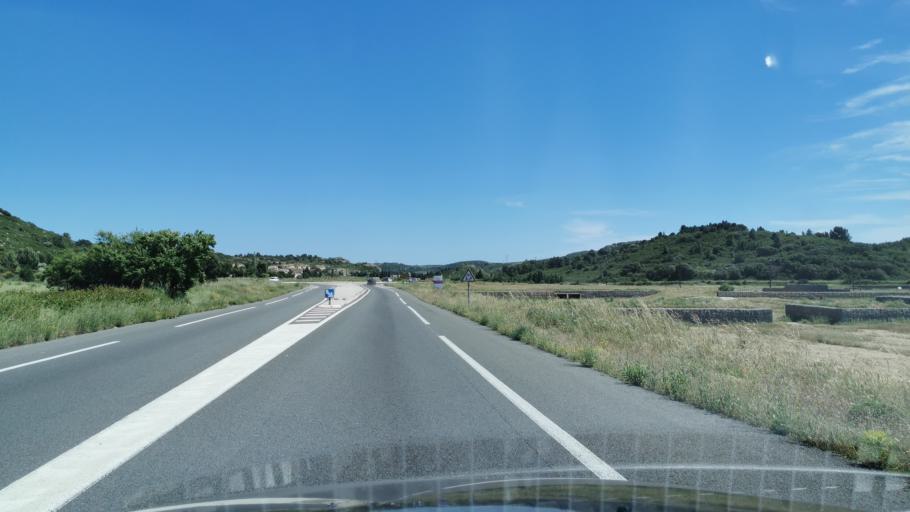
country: FR
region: Languedoc-Roussillon
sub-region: Departement de l'Aude
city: Nevian
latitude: 43.1919
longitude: 2.9066
